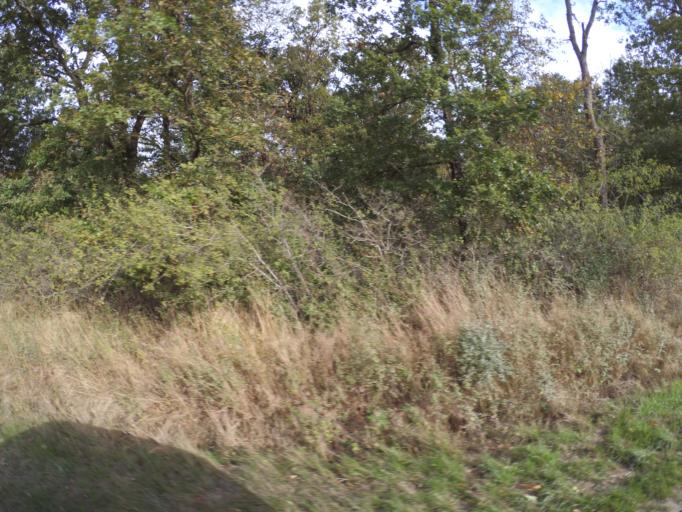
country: FR
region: Centre
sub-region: Departement d'Indre-et-Loire
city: Nazelles-Negron
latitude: 47.4670
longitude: 0.9389
